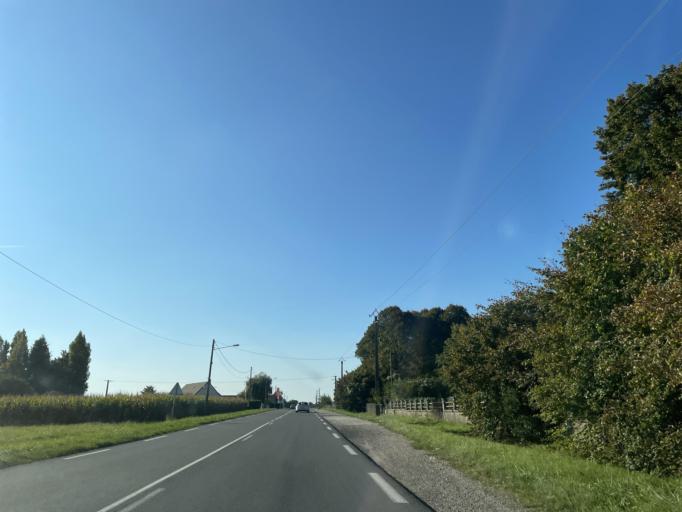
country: FR
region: Ile-de-France
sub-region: Departement de Seine-et-Marne
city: Pommeuse
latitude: 48.8298
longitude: 3.0217
